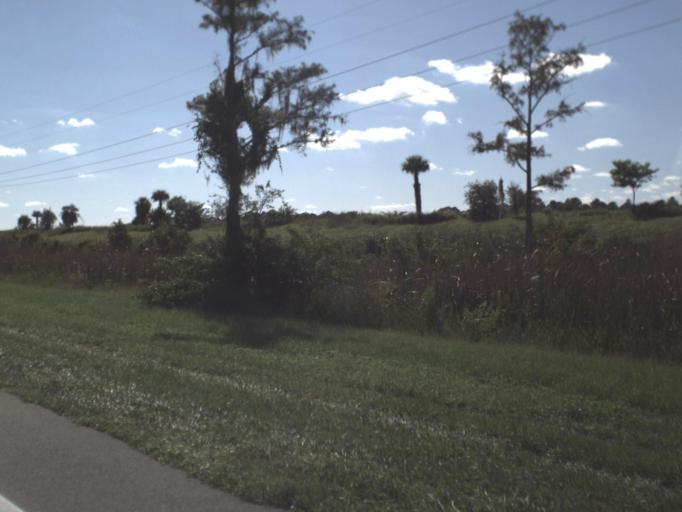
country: US
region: Florida
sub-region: Lee County
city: Lehigh Acres
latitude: 26.5306
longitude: -81.6114
